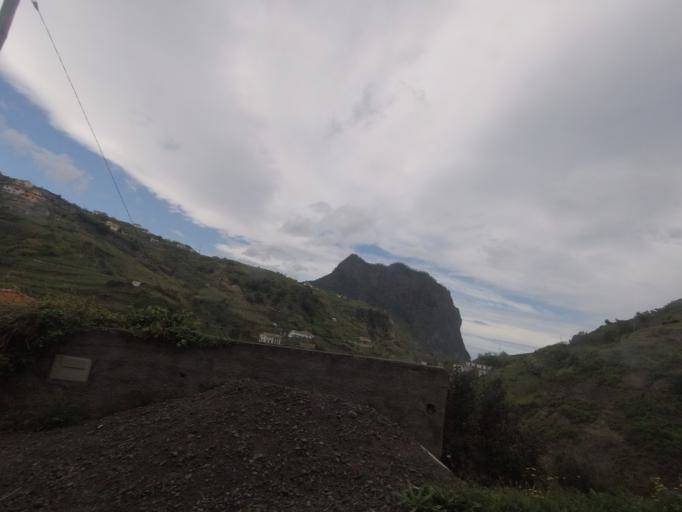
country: PT
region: Madeira
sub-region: Santana
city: Santana
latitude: 32.7648
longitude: -16.8212
